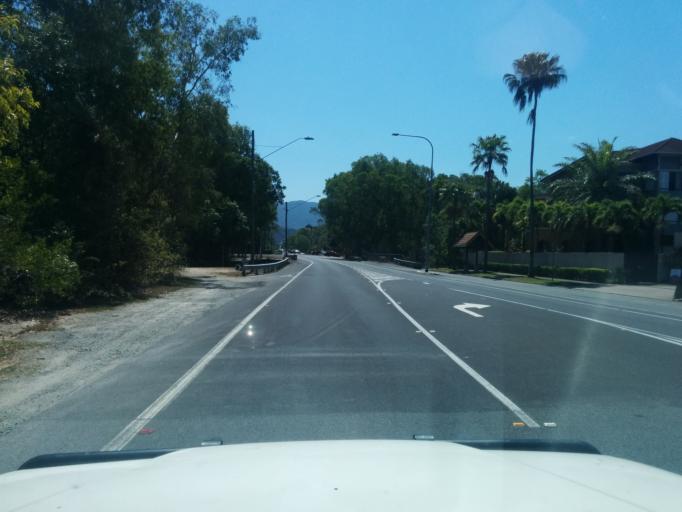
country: AU
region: Queensland
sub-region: Cairns
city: Cairns
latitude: -16.9043
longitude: 145.7546
